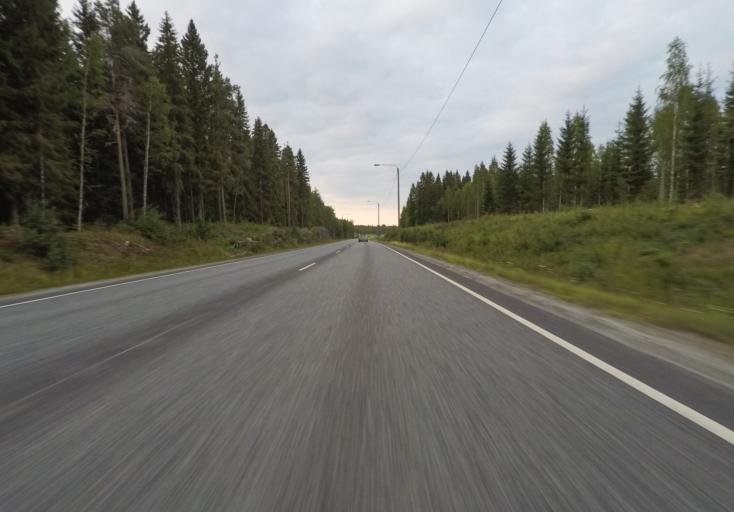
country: FI
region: Central Finland
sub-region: Jyvaeskylae
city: Hankasalmi
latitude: 62.3079
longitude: 26.4831
